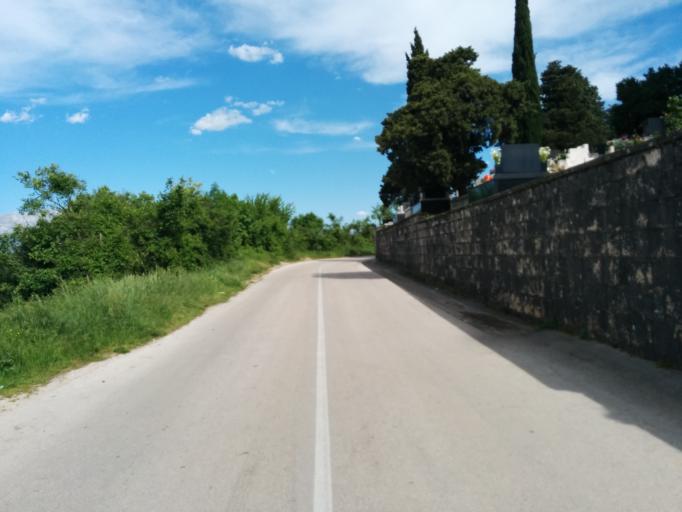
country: HR
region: Splitsko-Dalmatinska
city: Sinj
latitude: 43.7049
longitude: 16.6310
